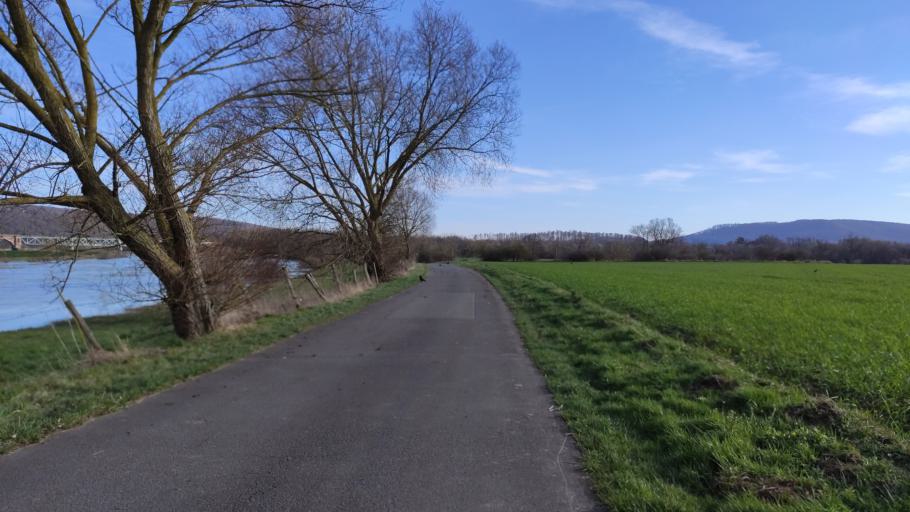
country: DE
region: Lower Saxony
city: Boffzen
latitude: 51.7411
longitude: 9.3749
